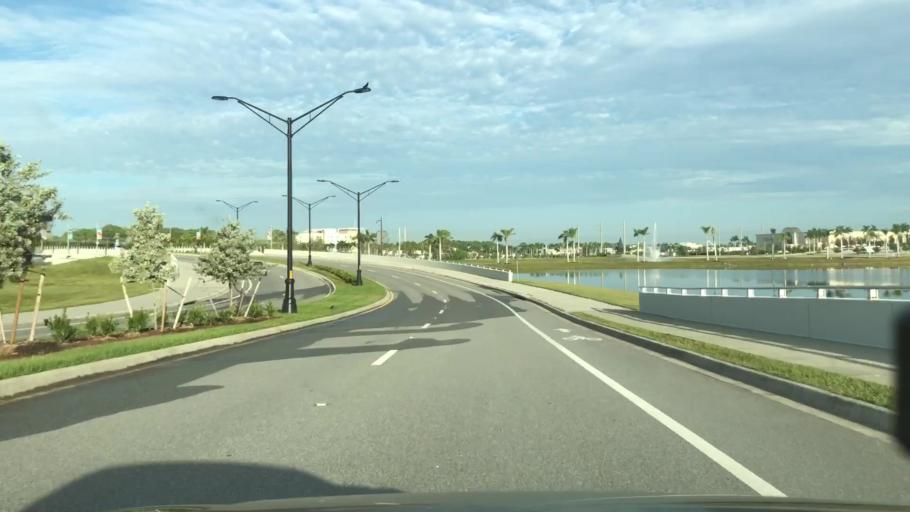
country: US
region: Florida
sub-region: Sarasota County
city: The Meadows
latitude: 27.3772
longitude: -82.4513
